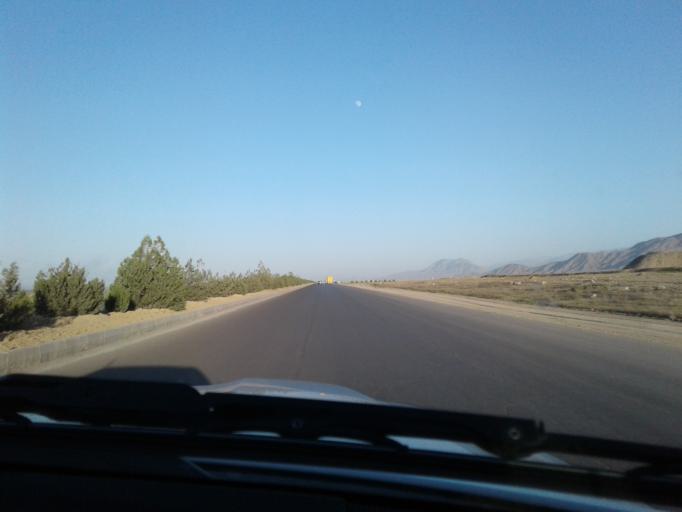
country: TM
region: Ahal
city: Baharly
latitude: 38.2320
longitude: 57.7826
